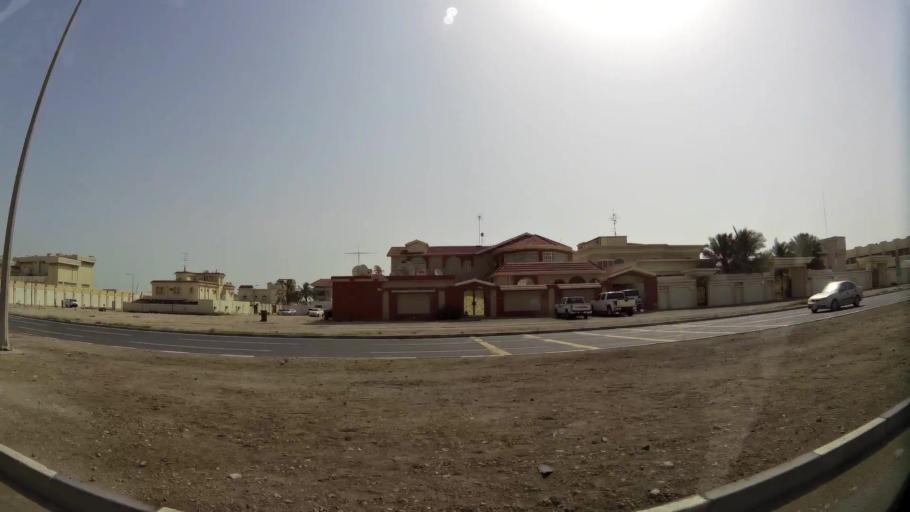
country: QA
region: Baladiyat ad Dawhah
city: Doha
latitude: 25.2453
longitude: 51.5241
